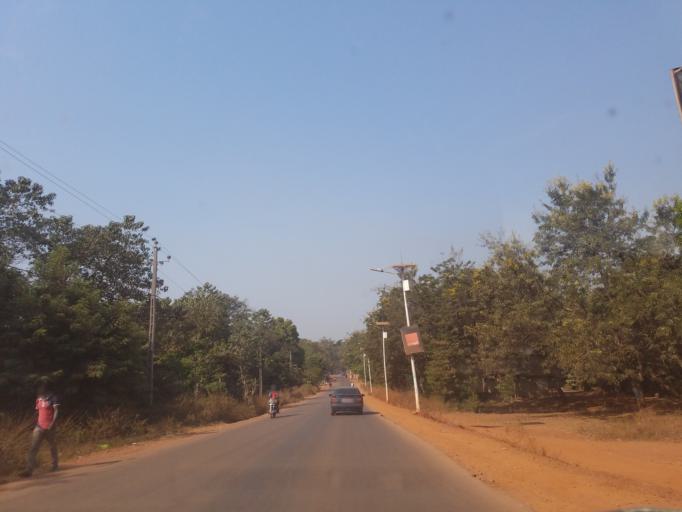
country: GN
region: Boke
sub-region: Boke Prefecture
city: Boke
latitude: 10.9204
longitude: -14.2954
